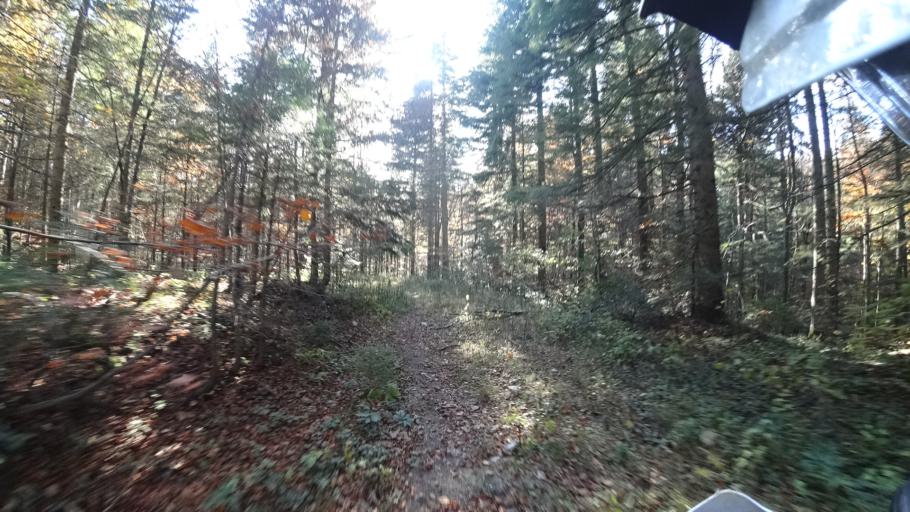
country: HR
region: Karlovacka
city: Plaski
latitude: 45.0469
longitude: 15.3241
